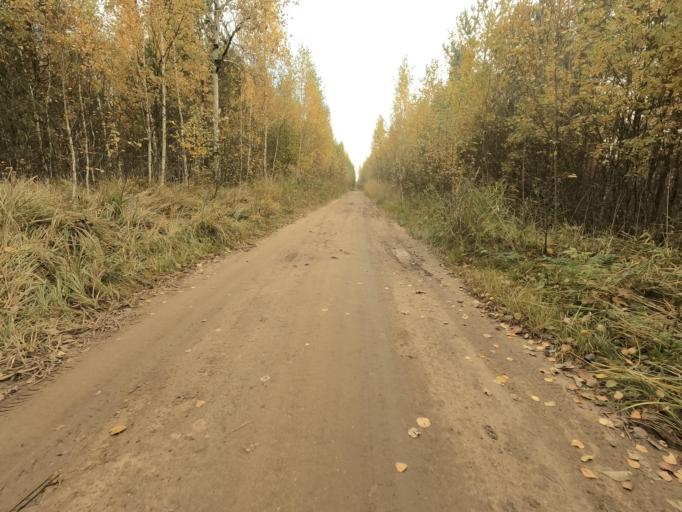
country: RU
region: Novgorod
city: Pankovka
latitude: 58.8772
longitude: 30.8655
